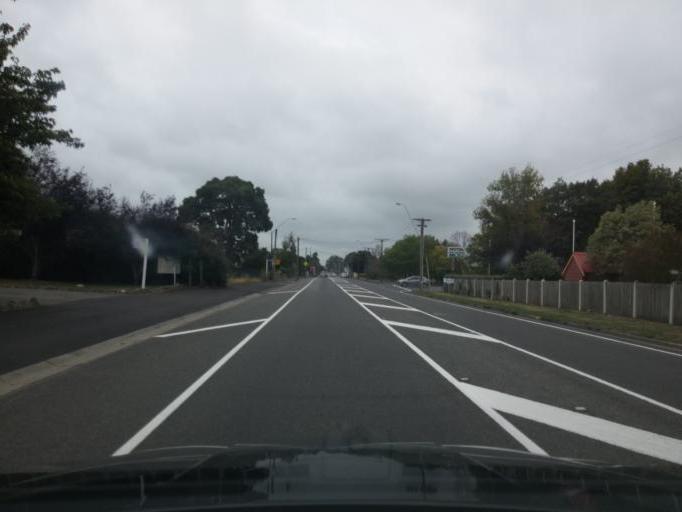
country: NZ
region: Wellington
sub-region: Masterton District
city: Masterton
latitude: -41.0898
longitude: 175.4499
